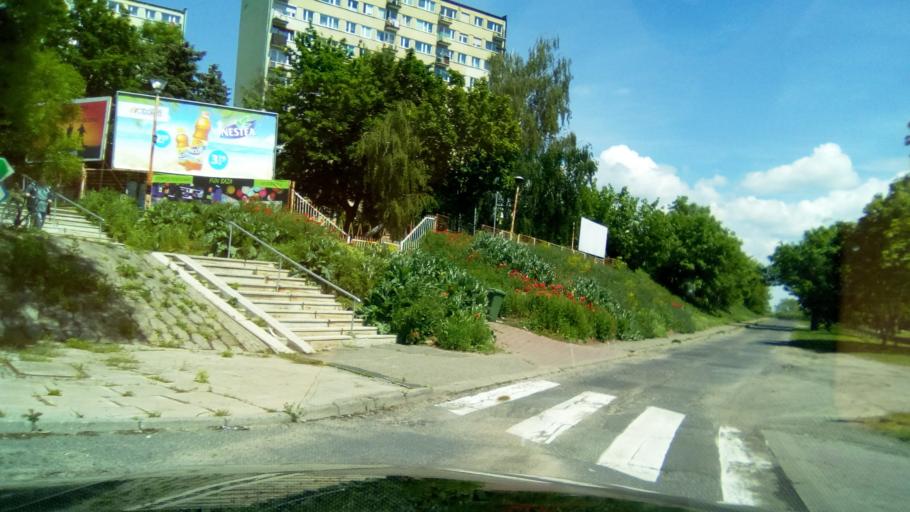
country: PL
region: Greater Poland Voivodeship
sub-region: Powiat gnieznienski
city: Gniezno
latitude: 52.5462
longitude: 17.6041
